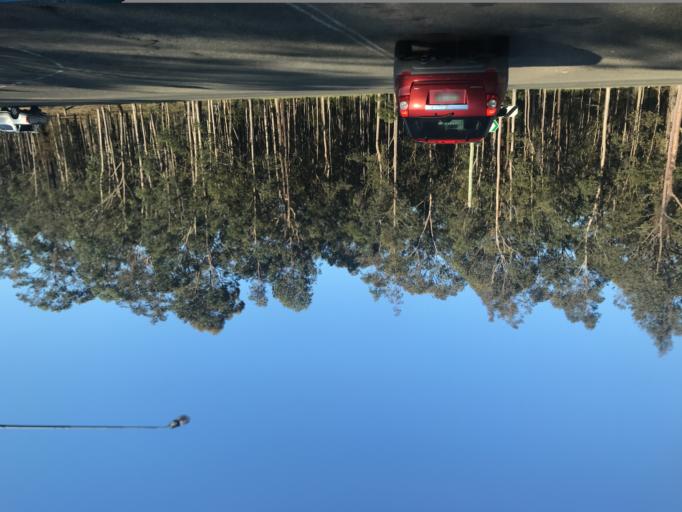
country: AU
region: New South Wales
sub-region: Cessnock
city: Cessnock
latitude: -32.8761
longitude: 151.3106
